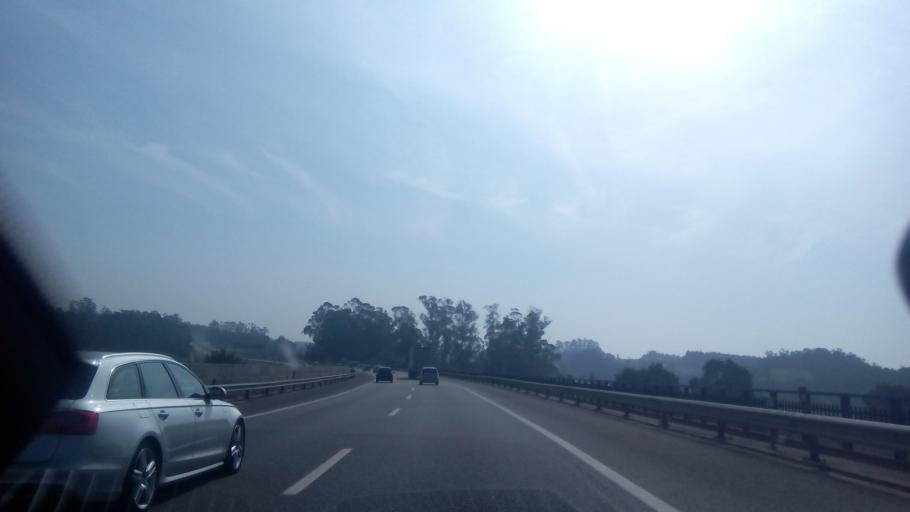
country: PT
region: Porto
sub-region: Vila do Conde
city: Vila do Conde
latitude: 41.3658
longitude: -8.7231
